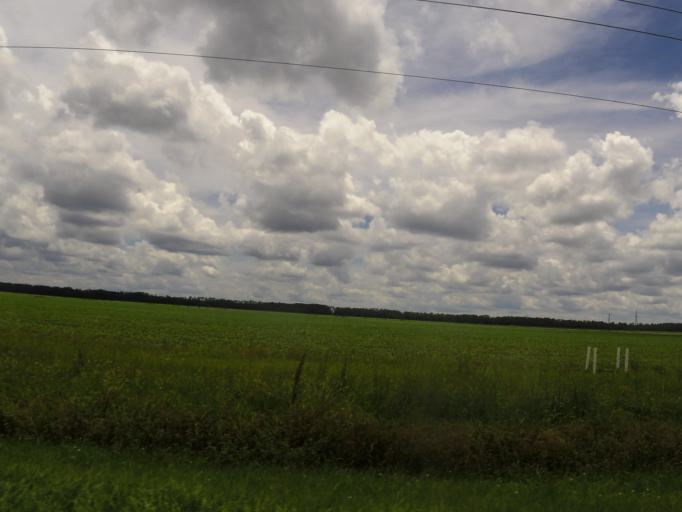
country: US
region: Florida
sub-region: Putnam County
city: East Palatka
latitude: 29.6784
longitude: -81.4366
